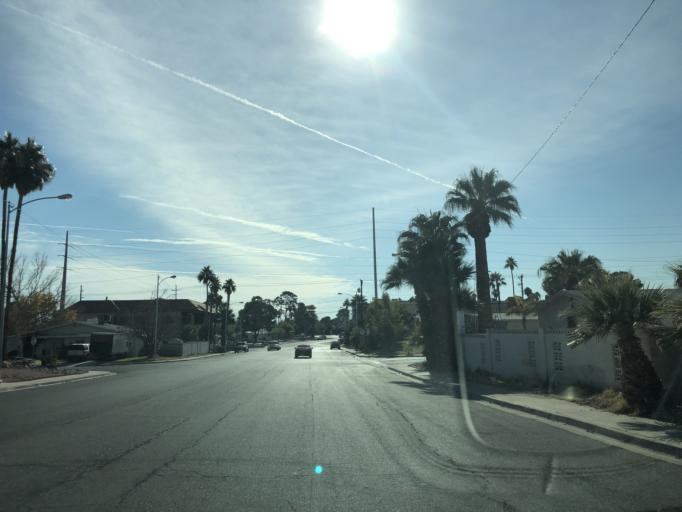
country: US
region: Nevada
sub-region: Clark County
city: Winchester
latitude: 36.1314
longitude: -115.1282
